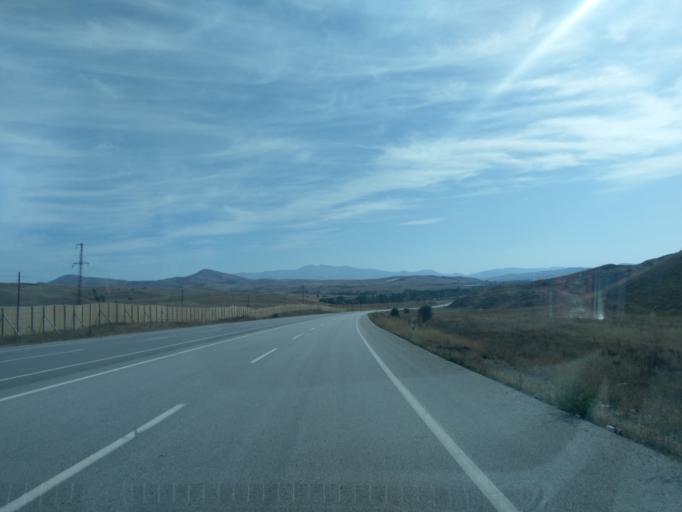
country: TR
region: Sivas
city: Imranli
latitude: 39.8838
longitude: 38.0497
